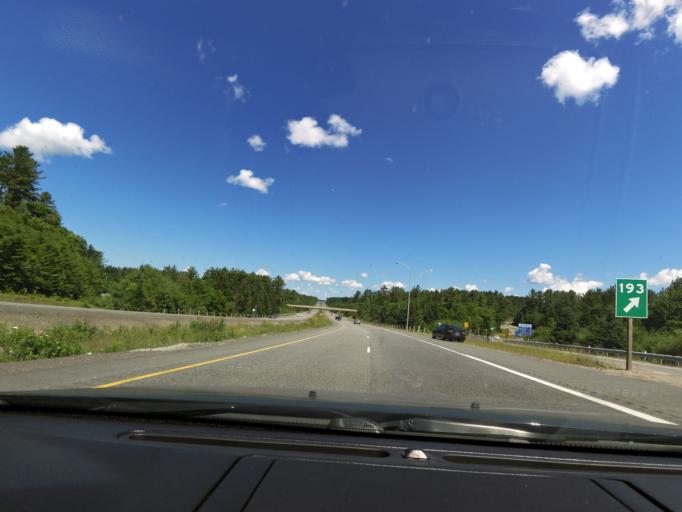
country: CA
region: Ontario
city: Bracebridge
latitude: 45.0835
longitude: -79.2967
